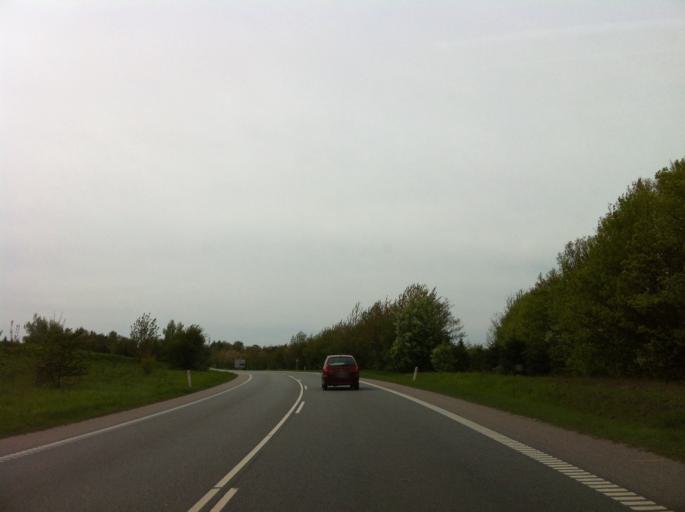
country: DK
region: Capital Region
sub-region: Egedal Kommune
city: Olstykke
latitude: 55.7747
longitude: 12.1492
